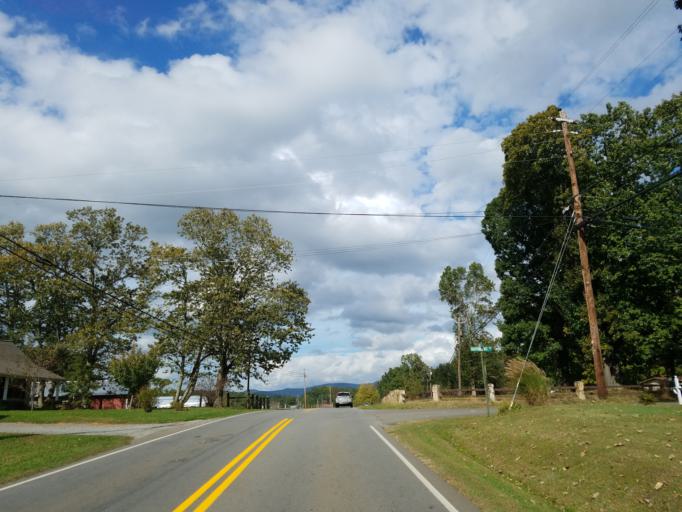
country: US
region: Georgia
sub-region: Pickens County
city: Jasper
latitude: 34.4394
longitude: -84.4224
